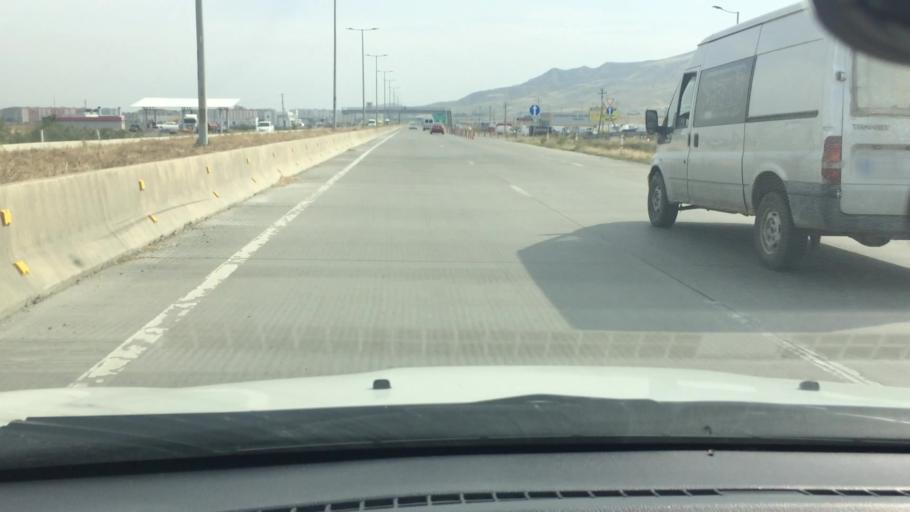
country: GE
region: Kvemo Kartli
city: Rust'avi
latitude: 41.5849
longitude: 44.9507
